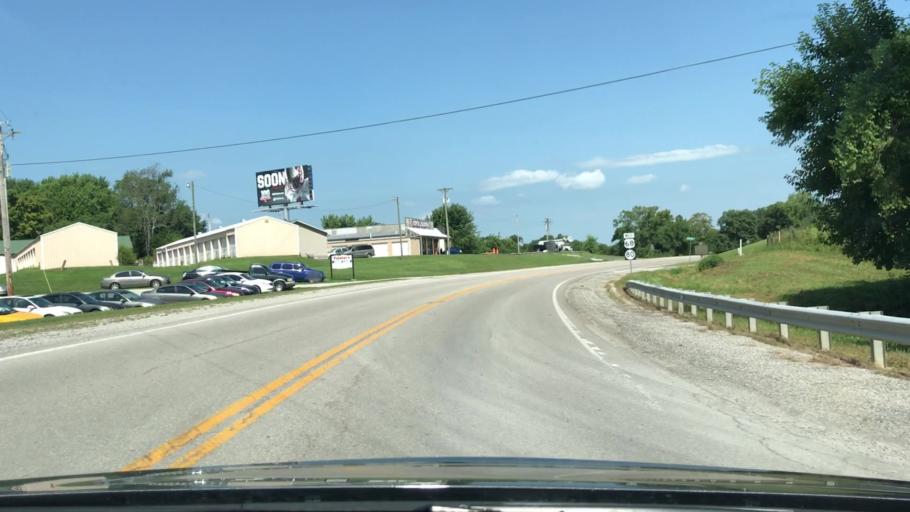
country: US
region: Kentucky
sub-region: Metcalfe County
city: Edmonton
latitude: 36.9890
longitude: -85.6550
